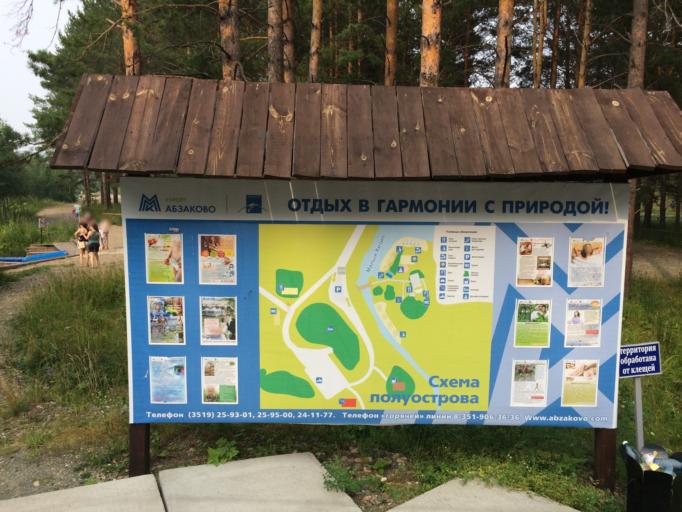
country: RU
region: Bashkortostan
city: Abzakovo
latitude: 53.7959
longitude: 58.6285
